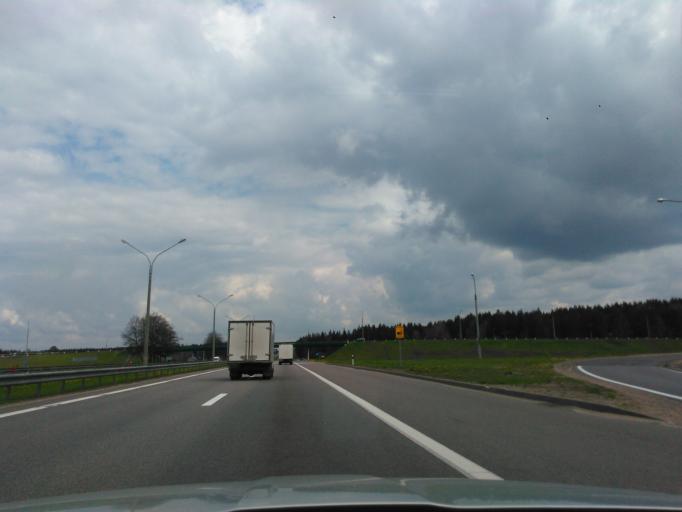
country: BY
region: Minsk
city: Korolev Stan
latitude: 53.9964
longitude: 27.8203
